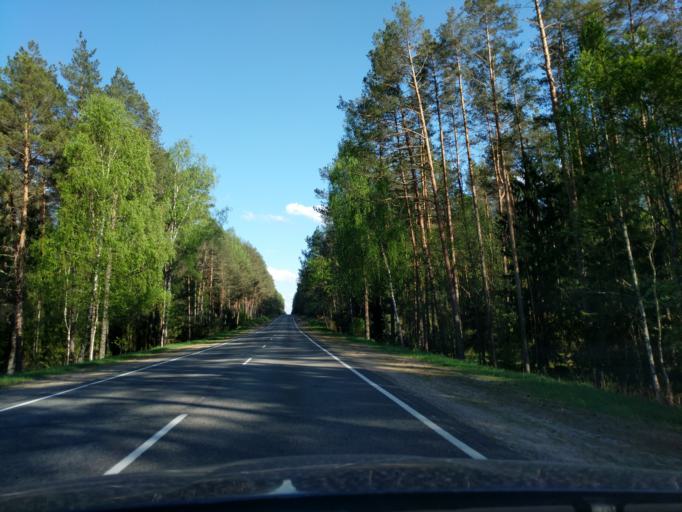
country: BY
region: Minsk
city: Myadzyel
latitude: 54.8035
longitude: 26.9967
